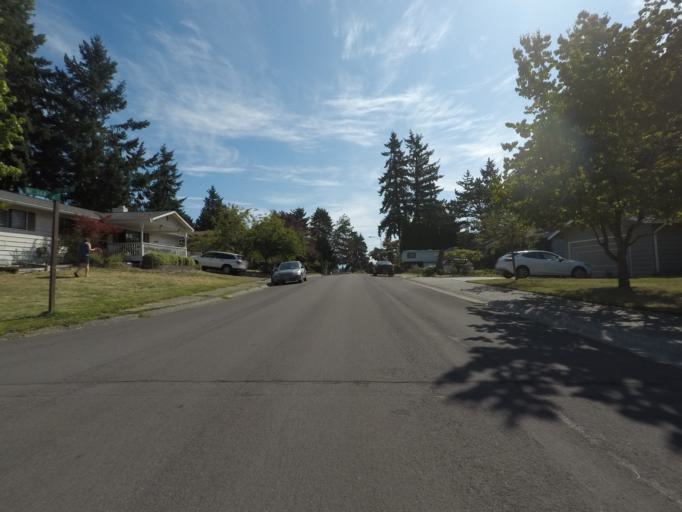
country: US
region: Washington
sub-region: King County
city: Inglewood-Finn Hill
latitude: 47.7319
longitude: -122.2308
